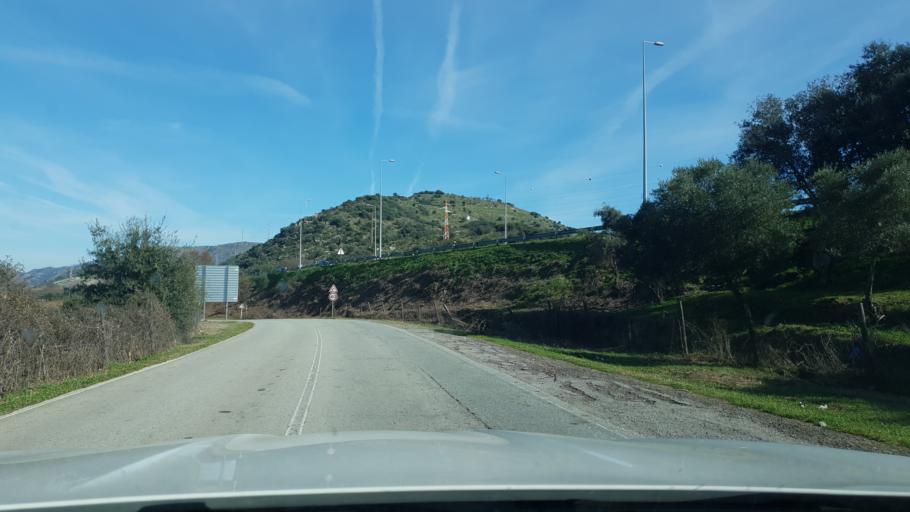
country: PT
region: Braganca
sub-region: Torre de Moncorvo
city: Torre de Moncorvo
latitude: 41.1815
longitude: -7.1036
